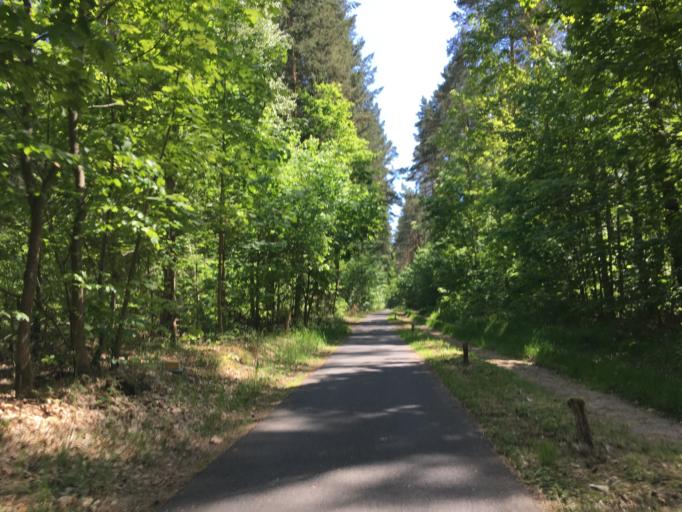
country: DE
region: Brandenburg
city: Chorin
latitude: 52.8515
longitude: 13.8754
